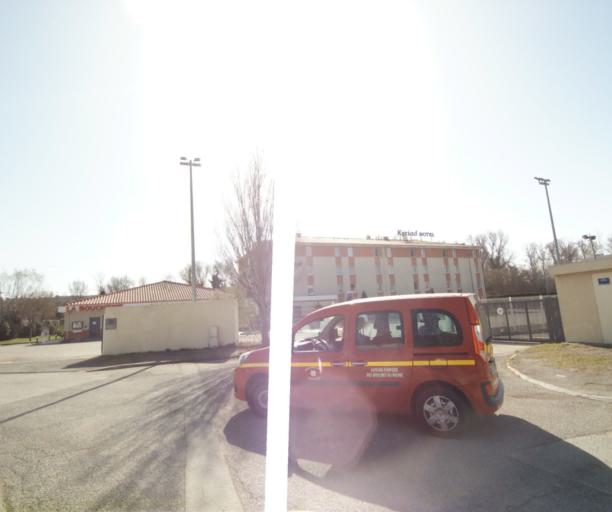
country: FR
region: Provence-Alpes-Cote d'Azur
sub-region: Departement des Bouches-du-Rhone
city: Cabries
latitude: 43.4267
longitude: 5.3859
